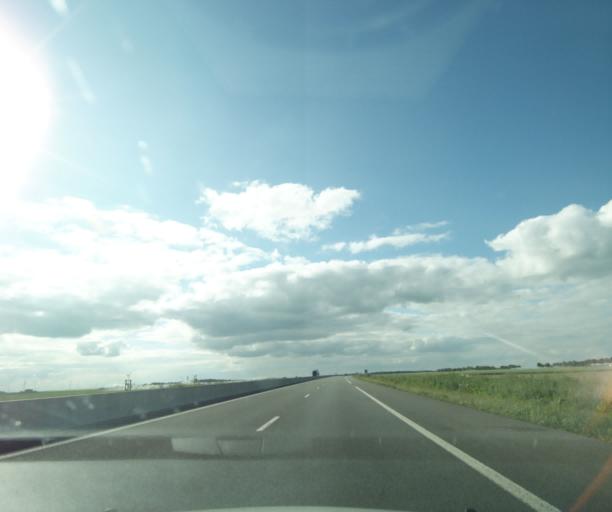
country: FR
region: Centre
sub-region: Departement d'Eure-et-Loir
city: Sours
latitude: 48.3664
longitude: 1.5959
